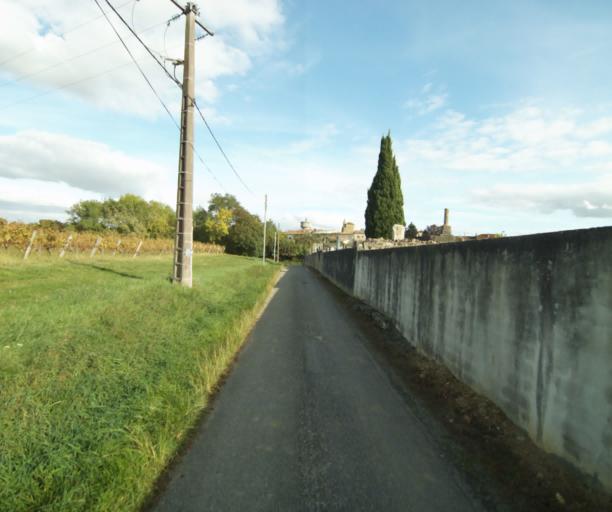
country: FR
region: Midi-Pyrenees
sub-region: Departement du Gers
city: Gondrin
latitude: 43.8877
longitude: 0.2351
